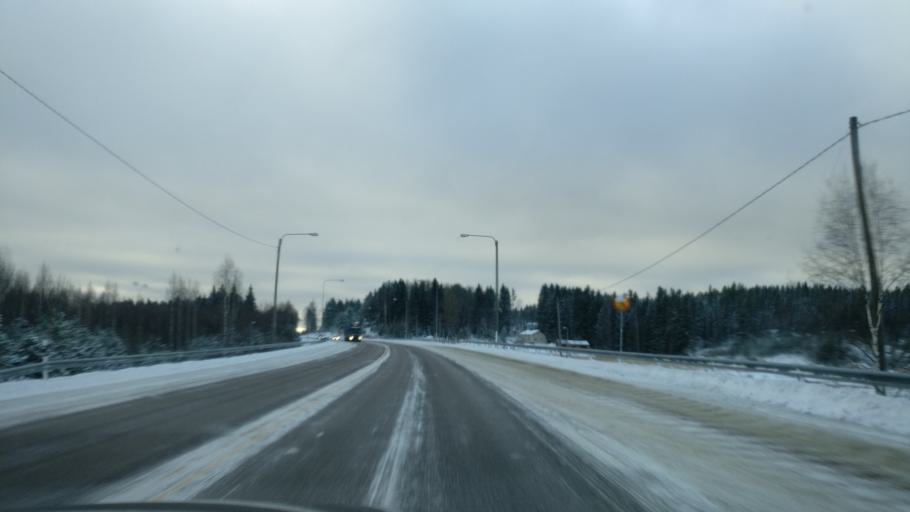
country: FI
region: Paijanne Tavastia
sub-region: Lahti
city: Heinola
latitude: 61.3328
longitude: 26.1661
